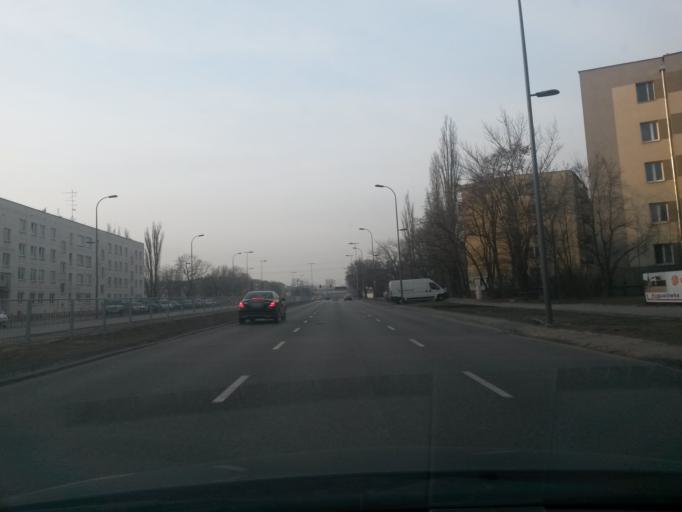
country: PL
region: Masovian Voivodeship
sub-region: Warszawa
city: Mokotow
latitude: 52.1911
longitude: 21.0589
